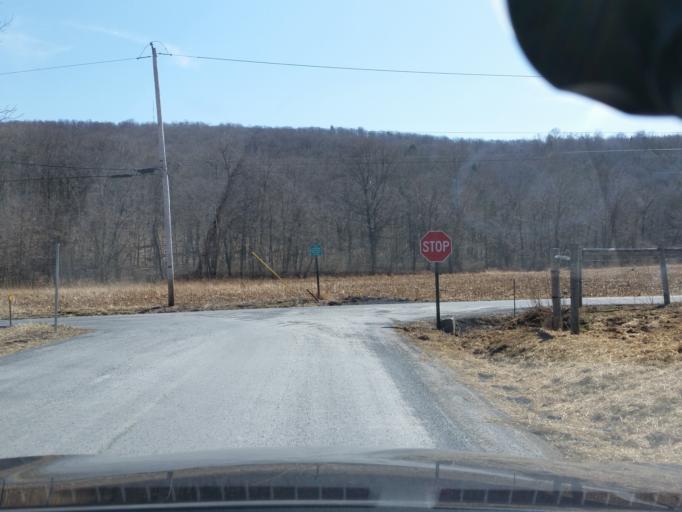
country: US
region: Pennsylvania
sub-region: Perry County
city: Marysville
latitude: 40.3299
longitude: -76.9616
